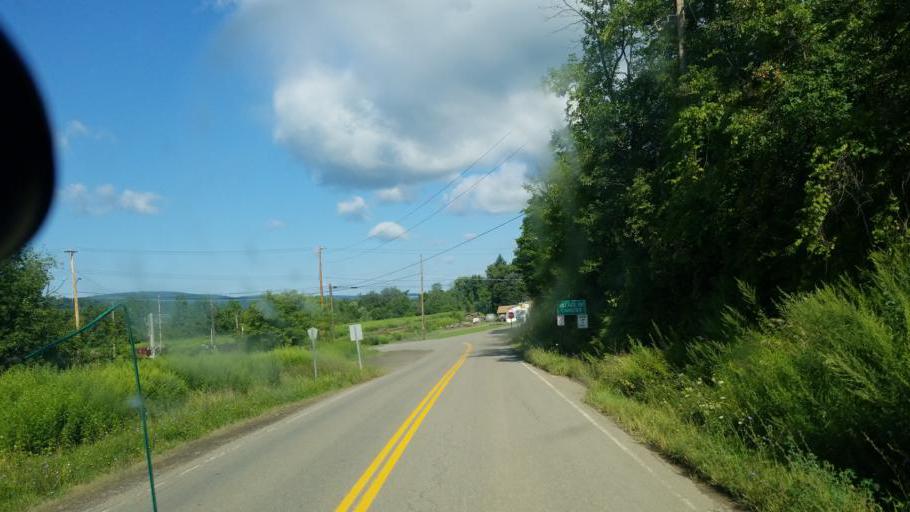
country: US
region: New York
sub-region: Steuben County
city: Canisteo
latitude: 42.2770
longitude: -77.5997
